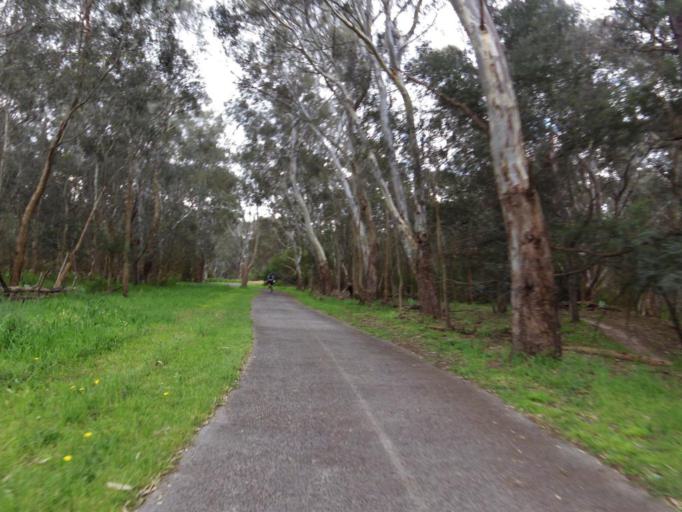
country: AU
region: Victoria
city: Ivanhoe East
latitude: -37.7822
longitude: 145.0596
